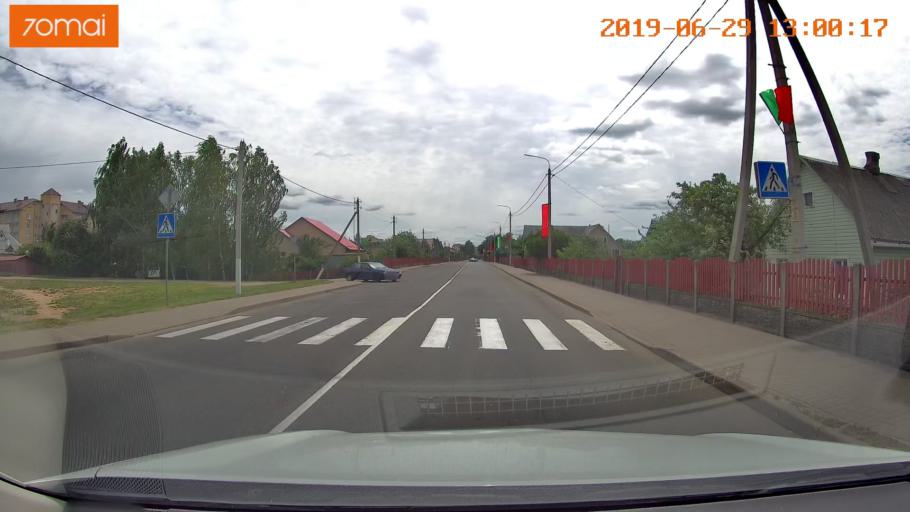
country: BY
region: Minsk
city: Slutsk
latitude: 53.0457
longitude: 27.5564
